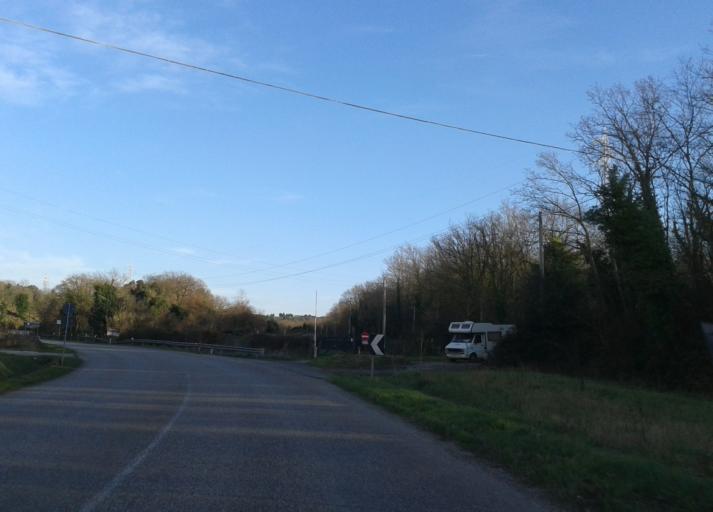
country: IT
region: Tuscany
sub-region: Provincia di Livorno
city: Guasticce
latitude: 43.5666
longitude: 10.3820
